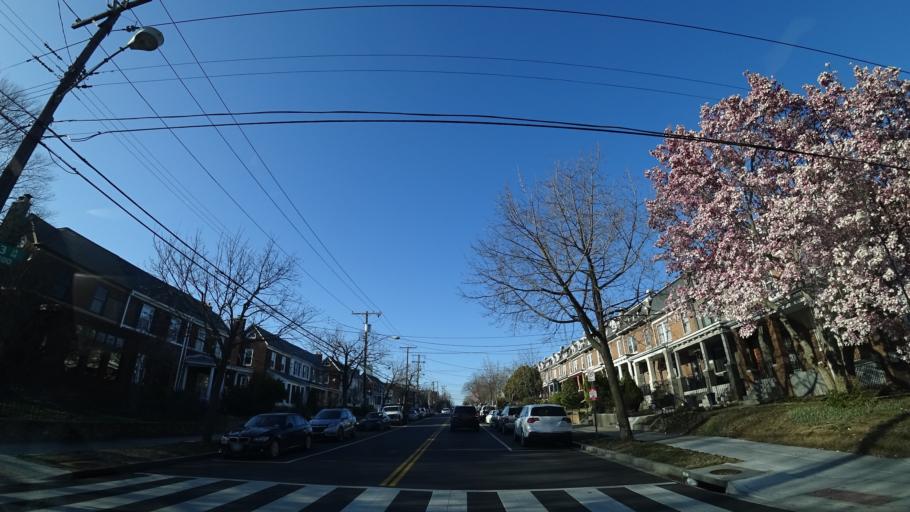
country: US
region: Maryland
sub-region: Montgomery County
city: Takoma Park
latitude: 38.9551
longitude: -77.0297
